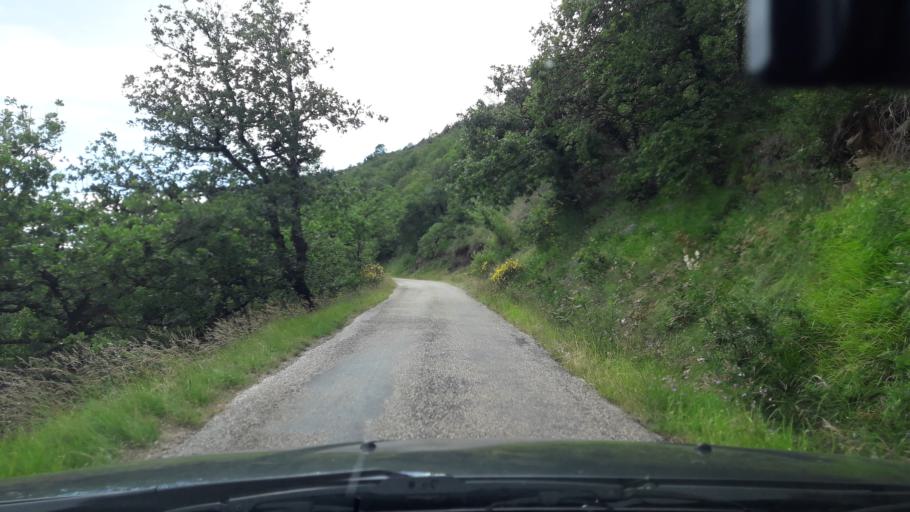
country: FR
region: Rhone-Alpes
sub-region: Departement de l'Ardeche
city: Alissas
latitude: 44.6815
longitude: 4.5916
